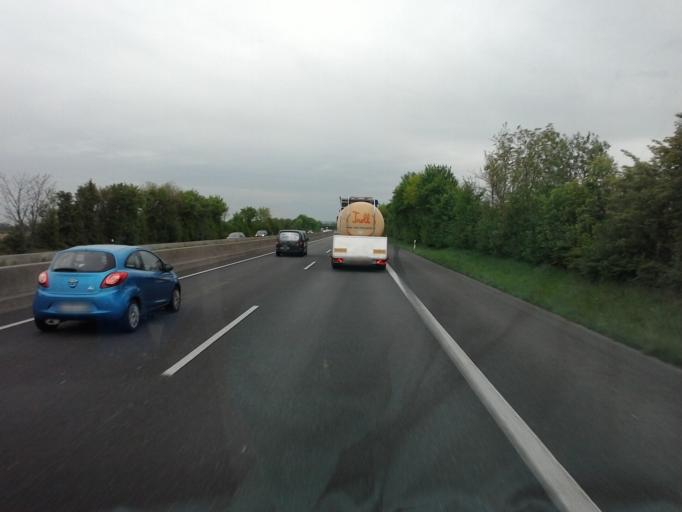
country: DE
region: North Rhine-Westphalia
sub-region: Regierungsbezirk Koln
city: Rheinbach
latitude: 50.7008
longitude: 6.9031
